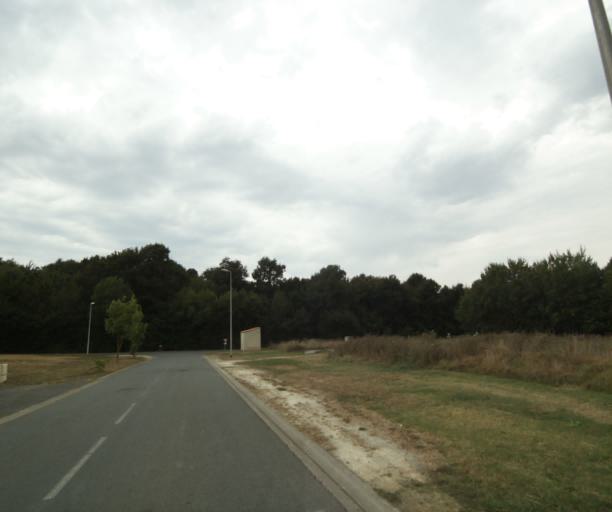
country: FR
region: Poitou-Charentes
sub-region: Departement de la Charente-Maritime
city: Tonnay-Charente
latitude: 45.9530
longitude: -0.8991
